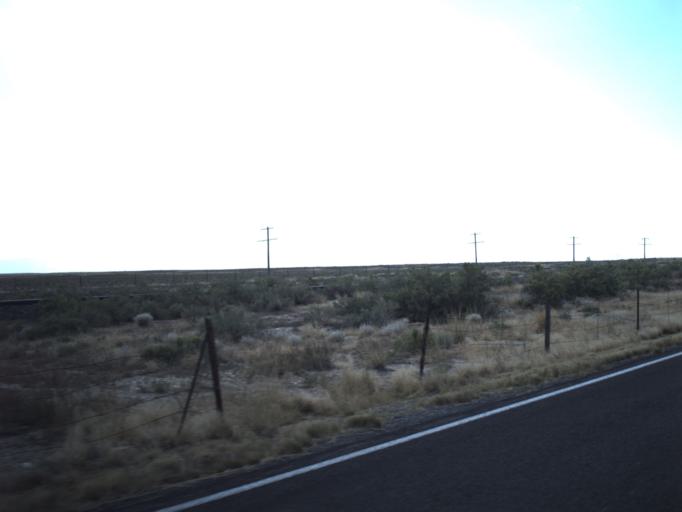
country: US
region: Utah
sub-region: Millard County
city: Delta
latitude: 38.9916
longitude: -112.7909
